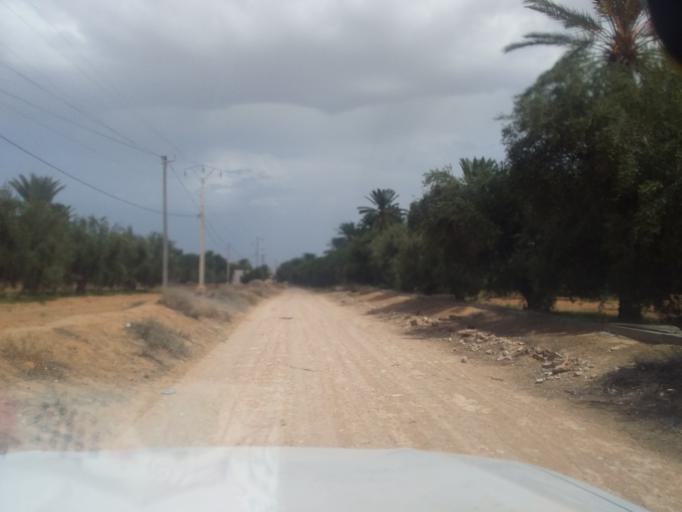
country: TN
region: Madanin
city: Medenine
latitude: 33.5972
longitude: 10.3248
